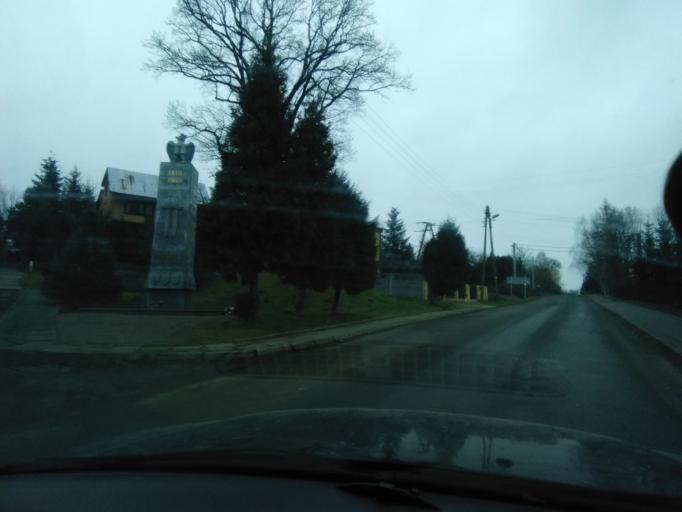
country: PL
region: Subcarpathian Voivodeship
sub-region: Powiat jaroslawski
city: Pruchnik
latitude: 49.9078
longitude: 22.5194
